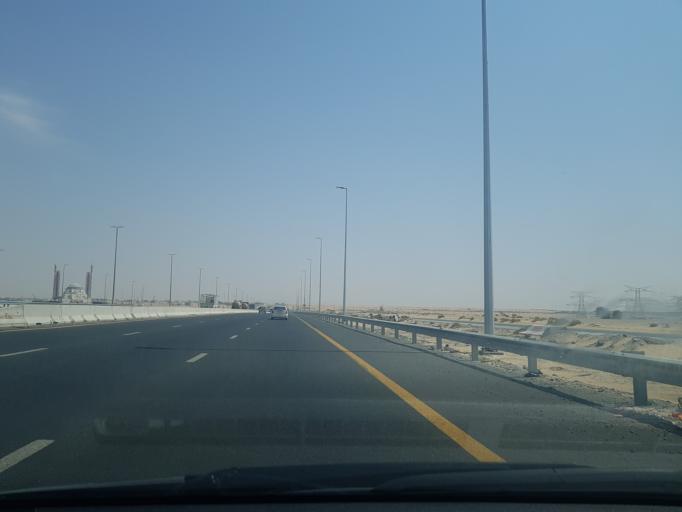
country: AE
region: Ash Shariqah
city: Sharjah
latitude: 25.2414
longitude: 55.5576
